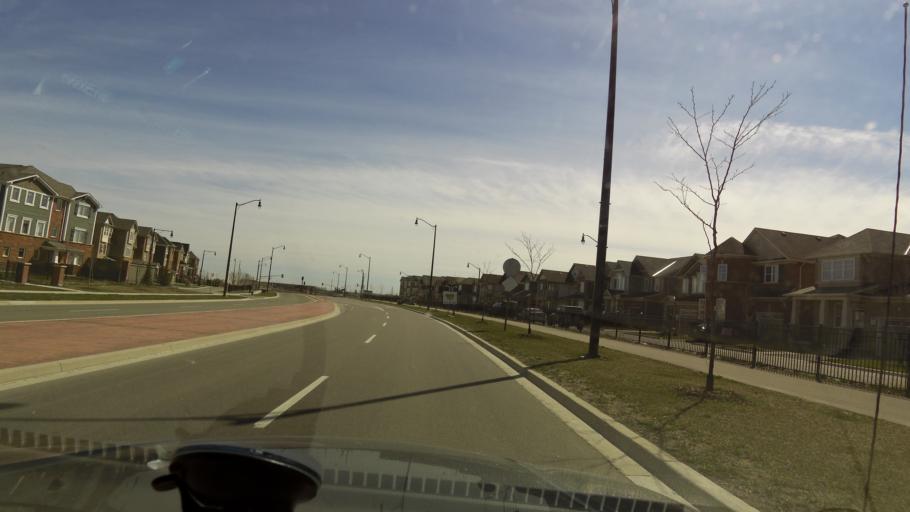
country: CA
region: Ontario
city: Brampton
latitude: 43.6778
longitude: -79.8293
